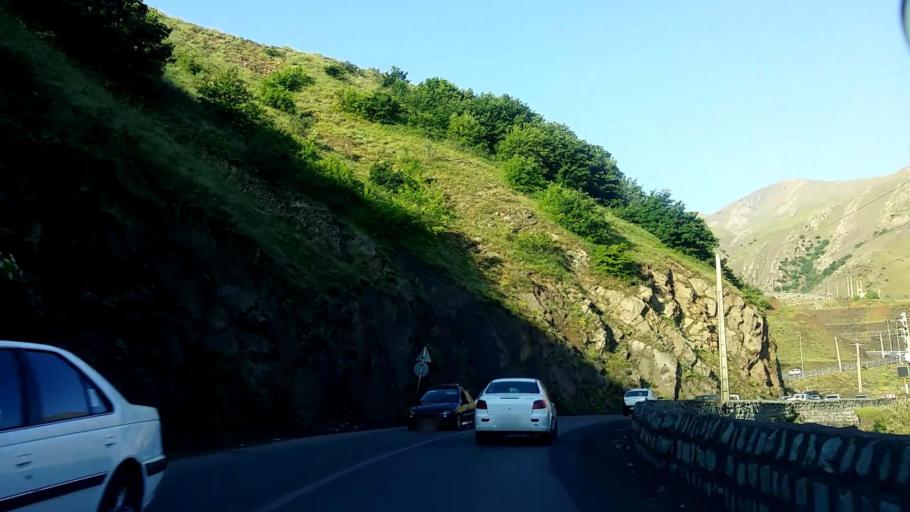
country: IR
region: Tehran
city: Tajrish
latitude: 36.2000
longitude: 51.3273
